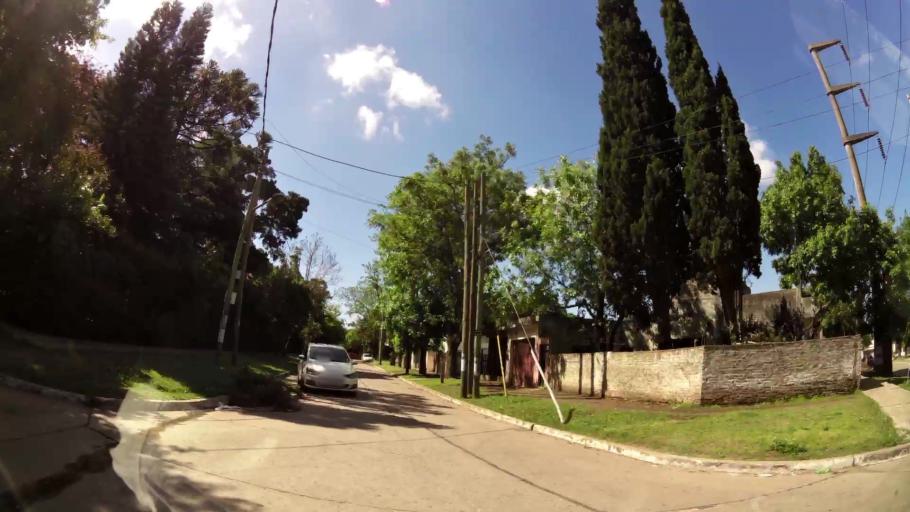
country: AR
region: Buenos Aires
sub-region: Partido de Quilmes
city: Quilmes
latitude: -34.8158
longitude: -58.2714
